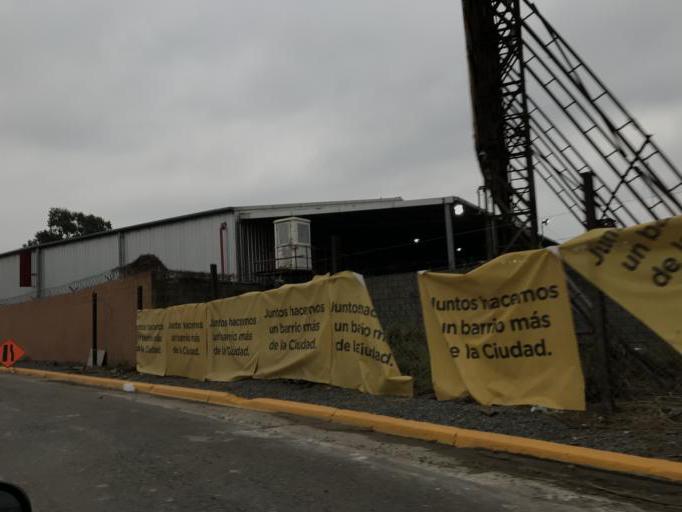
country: AR
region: Buenos Aires F.D.
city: Retiro
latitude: -34.5753
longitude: -58.3901
